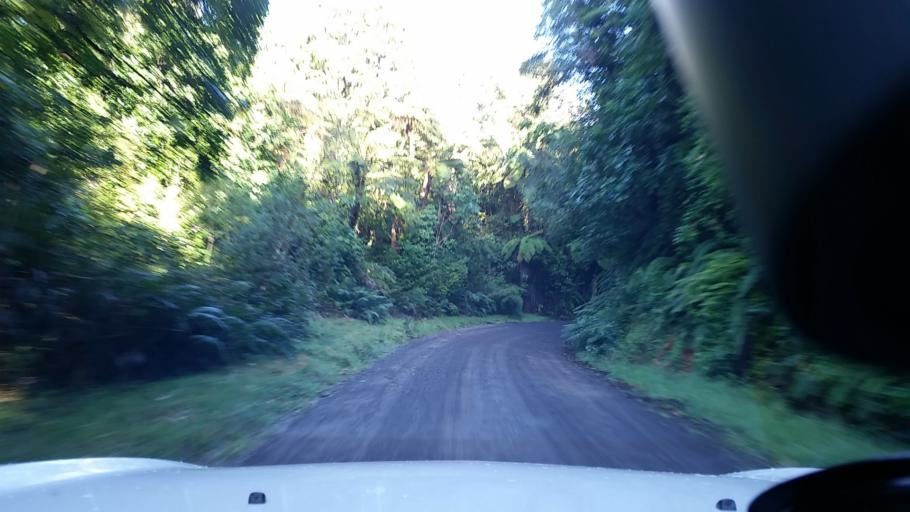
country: NZ
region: Bay of Plenty
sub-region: Kawerau District
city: Kawerau
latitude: -38.0222
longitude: 176.5687
